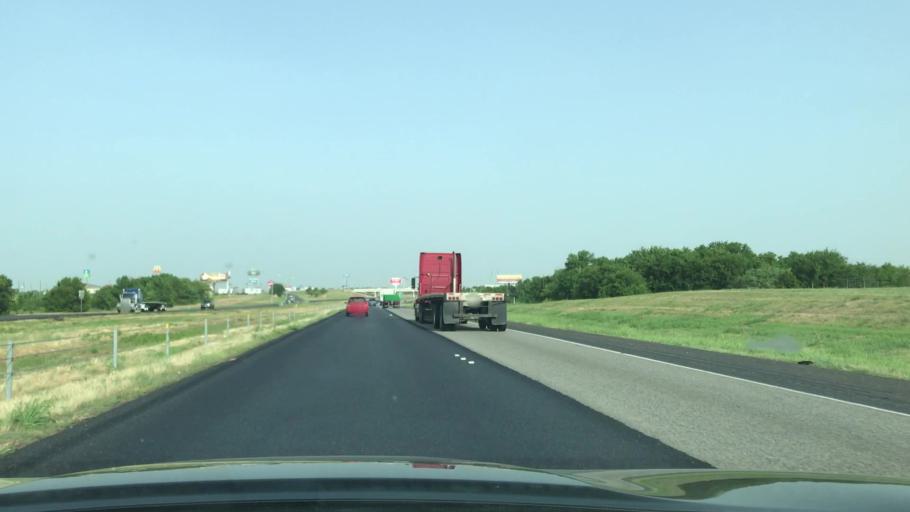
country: US
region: Texas
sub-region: Kaufman County
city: Terrell
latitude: 32.6990
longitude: -96.2672
